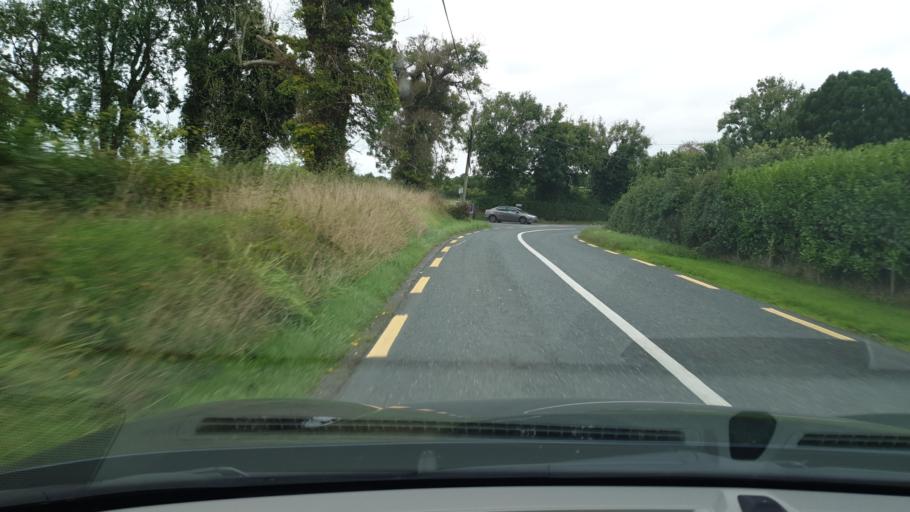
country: IE
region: Leinster
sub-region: Kildare
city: Kilcock
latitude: 53.4505
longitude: -6.6460
